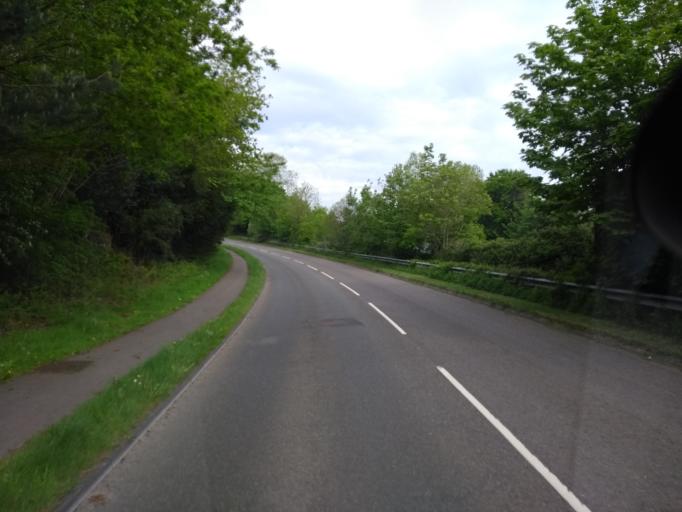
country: GB
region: England
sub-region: Dorset
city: Lyme Regis
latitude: 50.7412
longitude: -2.9157
